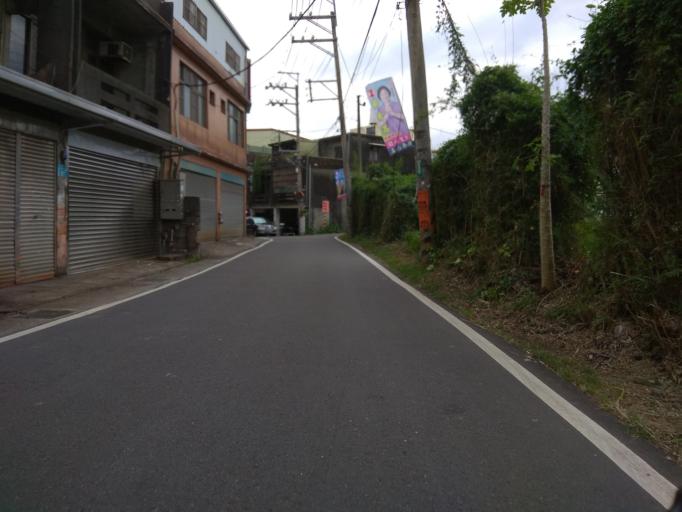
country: TW
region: Taiwan
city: Daxi
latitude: 24.9314
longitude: 121.2047
